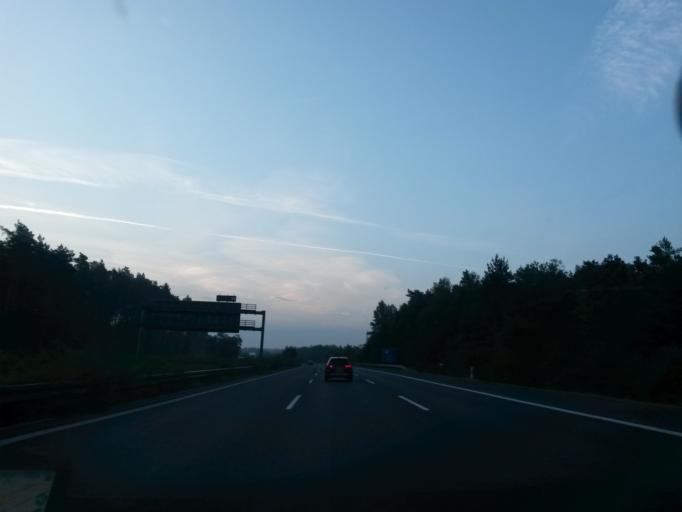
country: DE
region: Bavaria
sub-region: Regierungsbezirk Mittelfranken
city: Wendelstein
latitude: 49.3697
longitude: 11.1667
